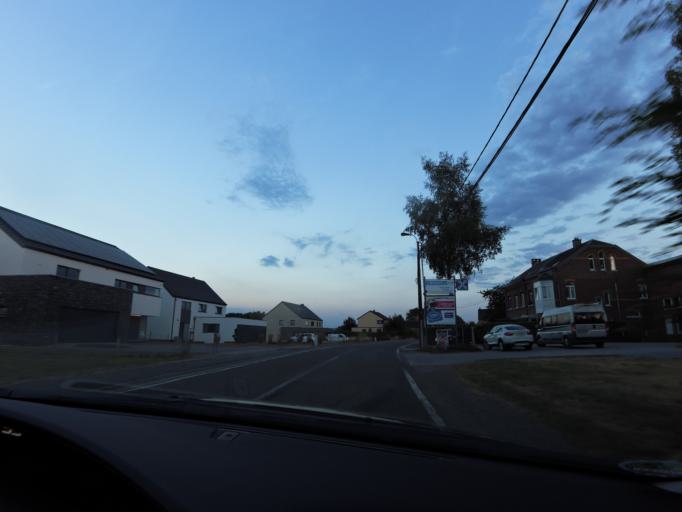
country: BE
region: Wallonia
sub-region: Province de Liege
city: La Calamine
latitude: 50.7115
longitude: 5.9850
